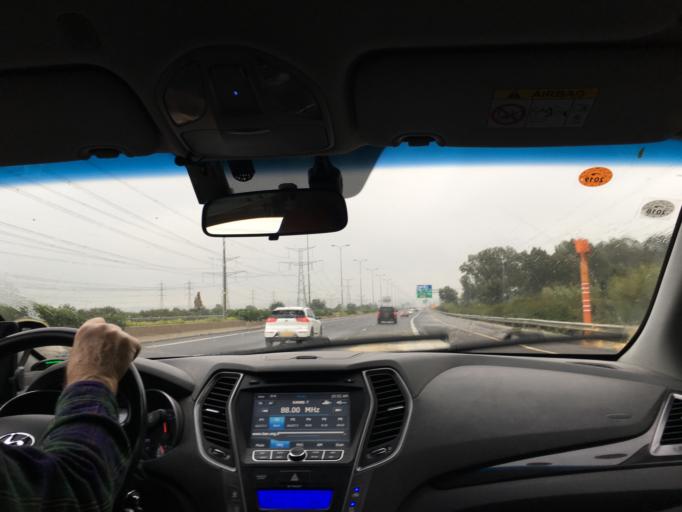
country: IL
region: Central District
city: Petah Tiqwa
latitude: 32.1201
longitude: 34.9120
